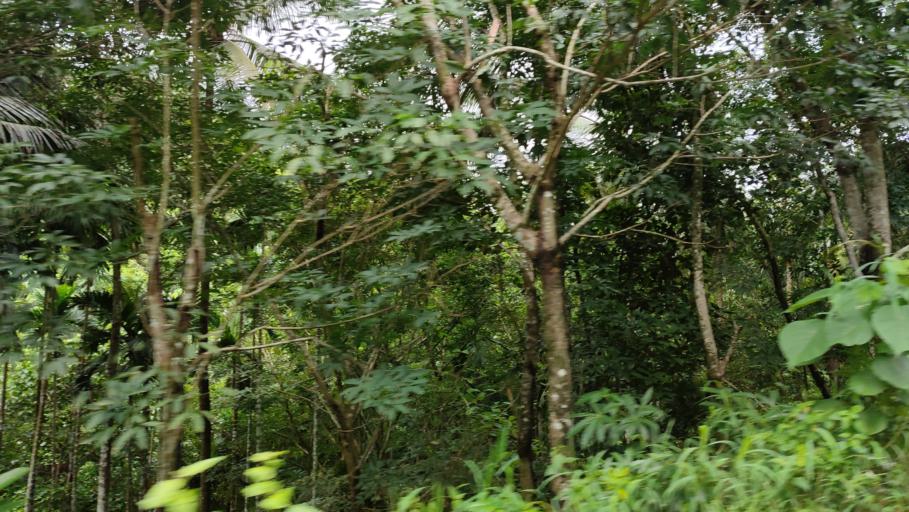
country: IN
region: Kerala
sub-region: Kasaragod District
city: Nileshwar
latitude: 12.2869
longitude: 75.2670
